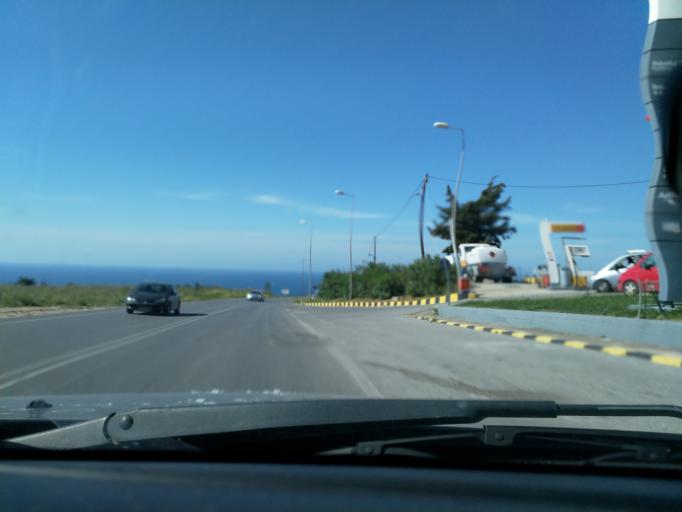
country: GR
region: Crete
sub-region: Nomos Rethymnis
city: Rethymno
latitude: 35.3531
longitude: 24.4612
